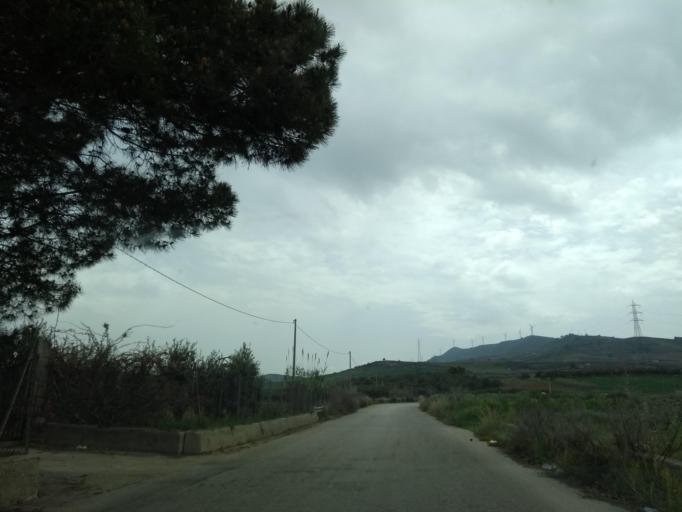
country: IT
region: Sicily
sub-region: Palermo
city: Partinico
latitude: 37.9916
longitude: 13.0679
